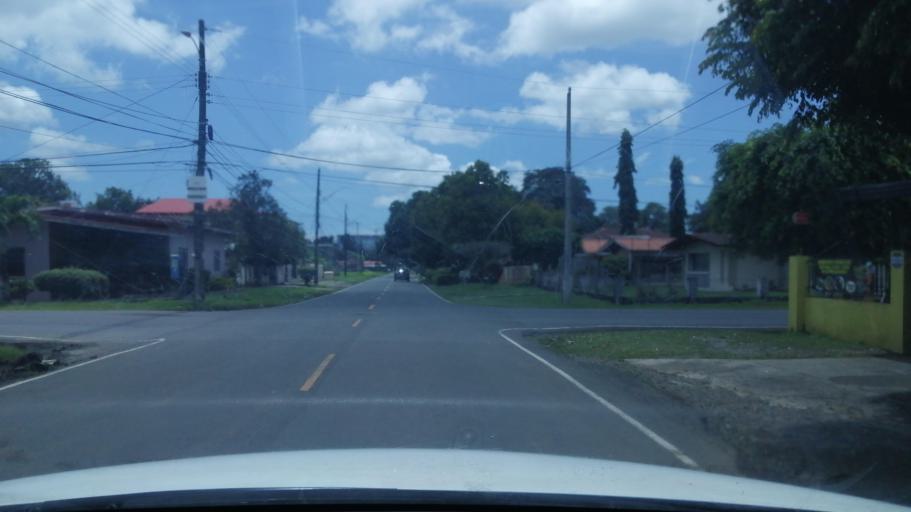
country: PA
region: Chiriqui
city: David
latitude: 8.4357
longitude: -82.4292
